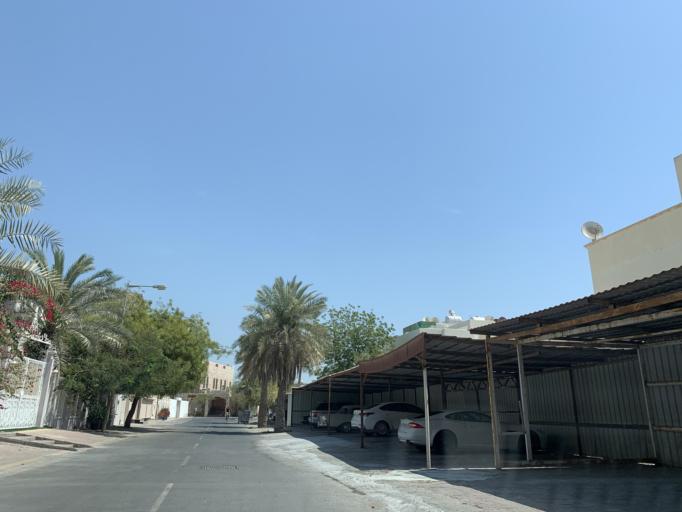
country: BH
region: Muharraq
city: Al Muharraq
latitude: 26.2745
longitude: 50.6081
